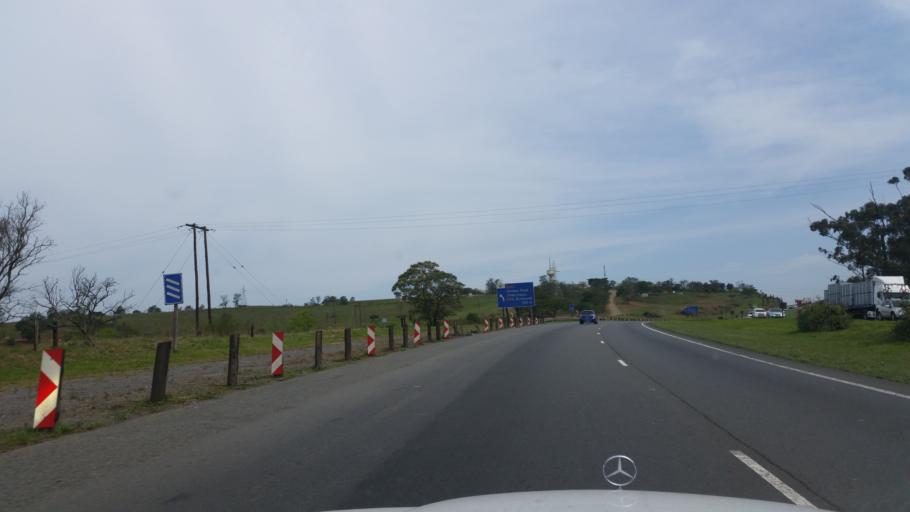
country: ZA
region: KwaZulu-Natal
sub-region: uMgungundlovu District Municipality
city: Camperdown
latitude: -29.7080
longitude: 30.4963
